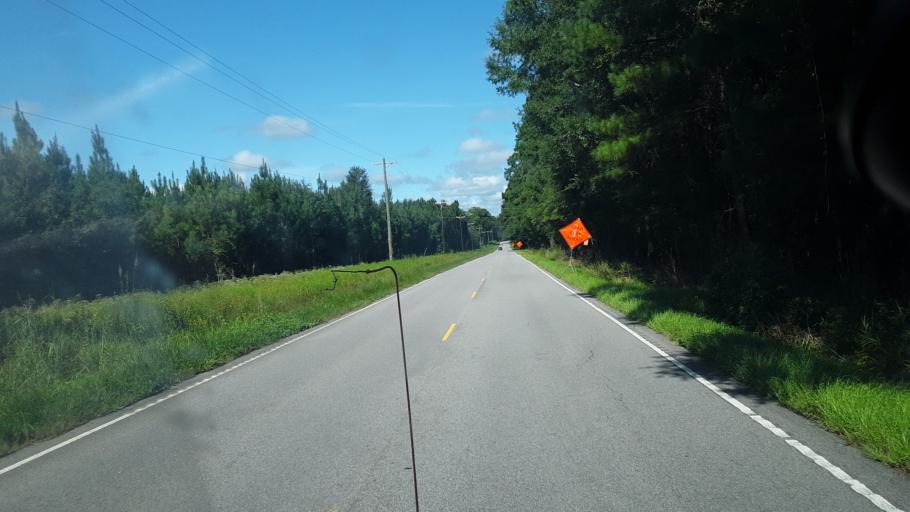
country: US
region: South Carolina
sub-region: Jasper County
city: Ridgeland
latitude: 32.5891
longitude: -80.9388
